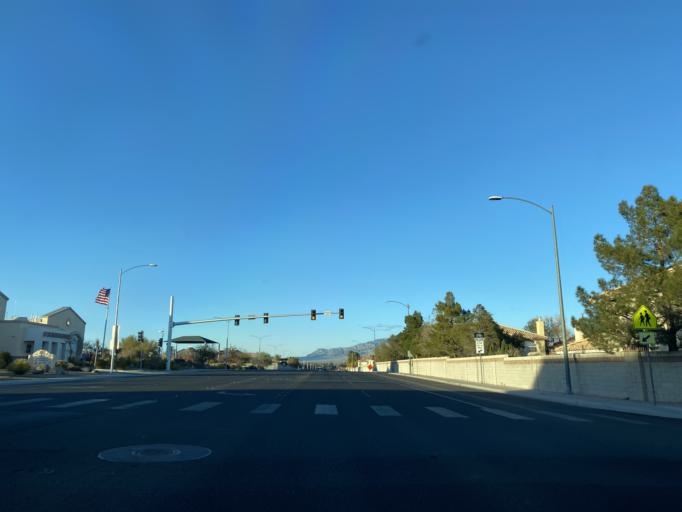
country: US
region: Nevada
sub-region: Clark County
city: Summerlin South
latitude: 36.2298
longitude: -115.2975
